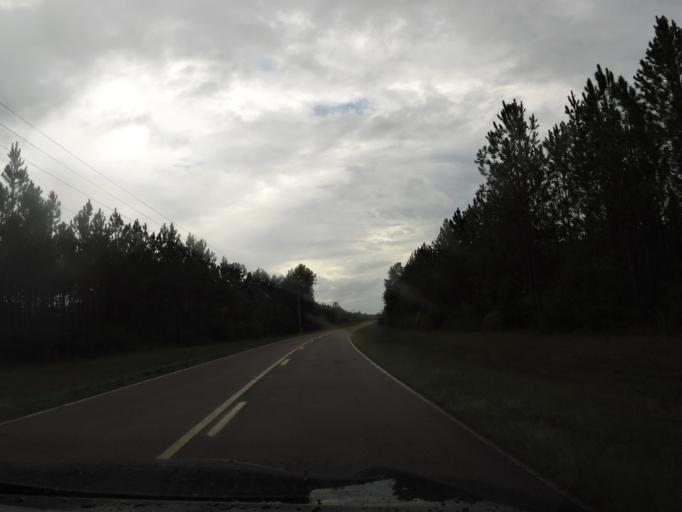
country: US
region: Florida
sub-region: Nassau County
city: Callahan
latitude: 30.5183
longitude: -81.9927
